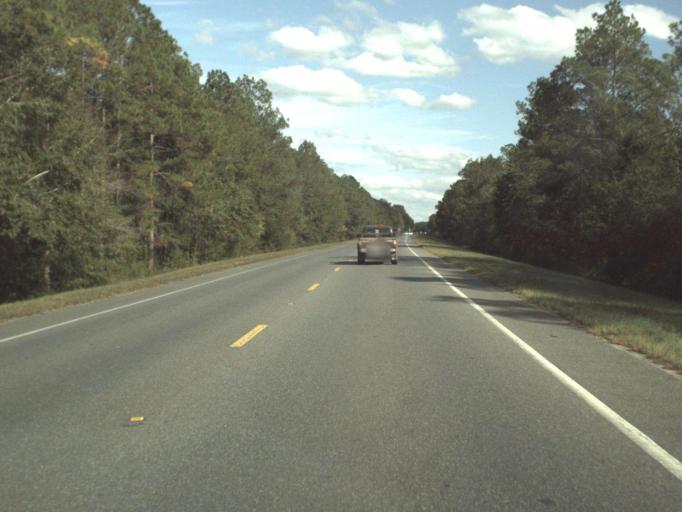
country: US
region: Florida
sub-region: Holmes County
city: Bonifay
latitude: 30.7791
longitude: -85.6233
